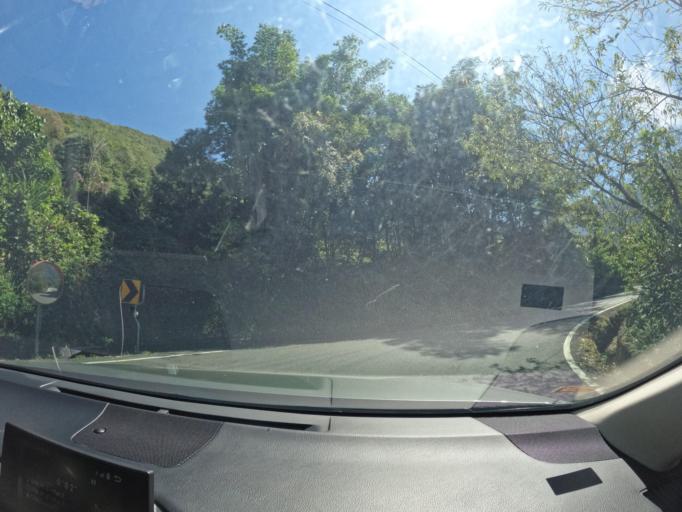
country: TW
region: Taiwan
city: Yujing
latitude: 23.2652
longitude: 120.8480
